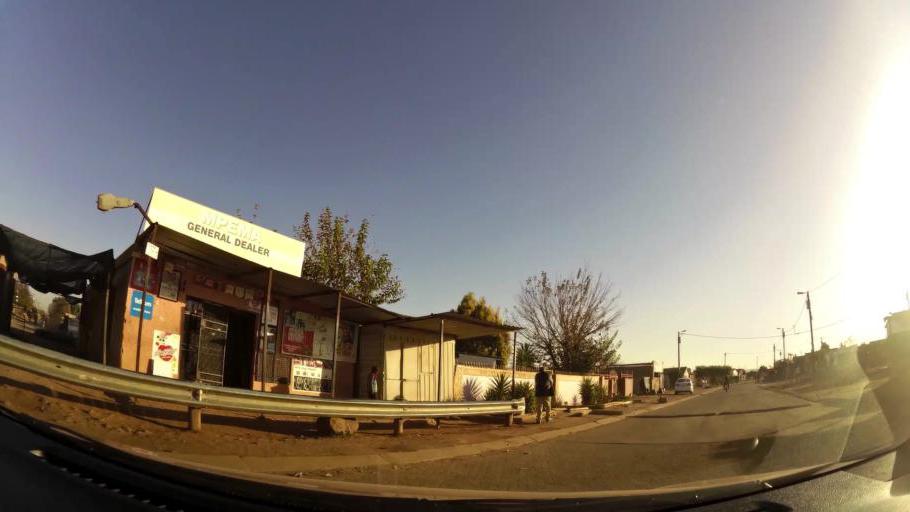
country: ZA
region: Gauteng
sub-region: City of Tshwane Metropolitan Municipality
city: Mabopane
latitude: -25.6007
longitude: 28.1042
